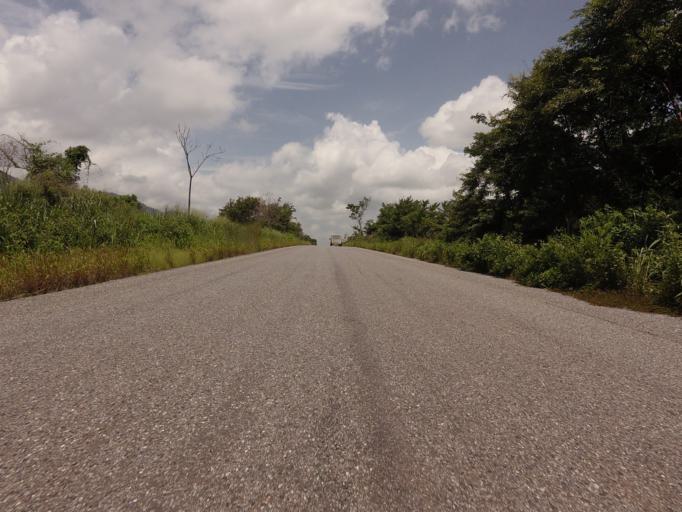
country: GH
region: Volta
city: Kpandu
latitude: 6.8380
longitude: 0.3839
